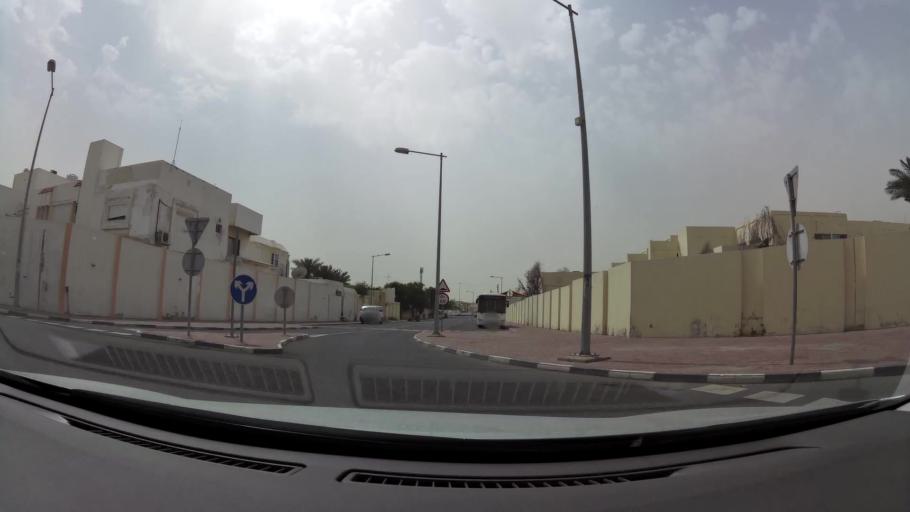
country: QA
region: Baladiyat ad Dawhah
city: Doha
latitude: 25.2585
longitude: 51.5276
